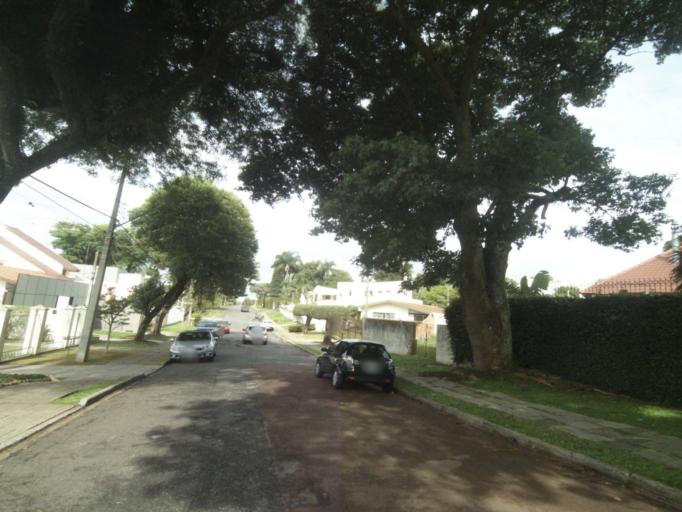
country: BR
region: Parana
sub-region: Curitiba
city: Curitiba
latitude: -25.4394
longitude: -49.2996
